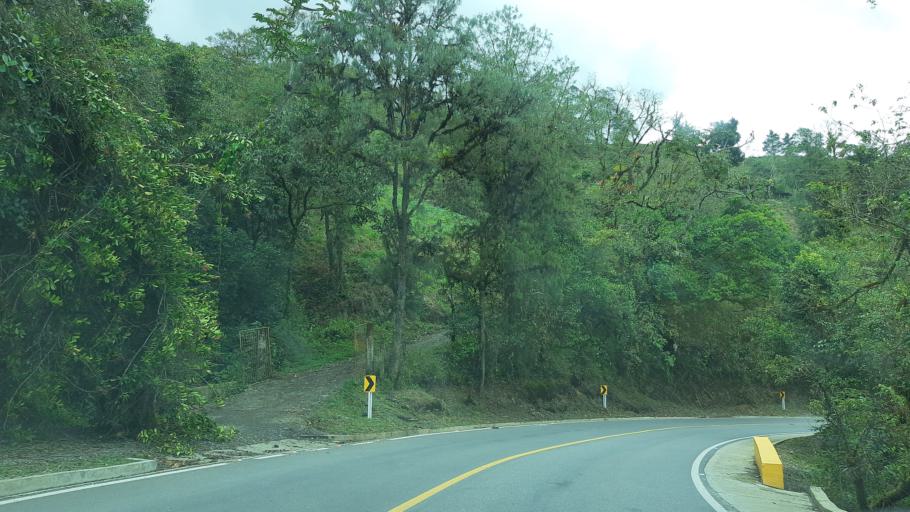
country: CO
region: Boyaca
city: Chivor
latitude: 4.9581
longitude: -73.3134
